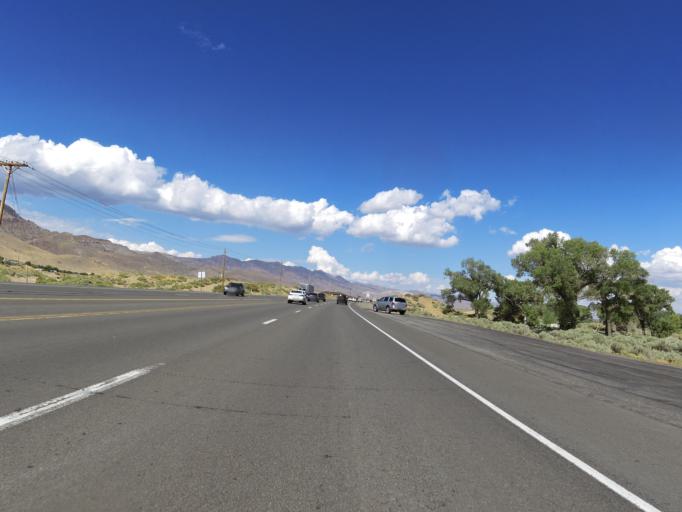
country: US
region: Nevada
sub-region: Lyon County
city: Dayton
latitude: 39.2550
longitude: -119.5866
